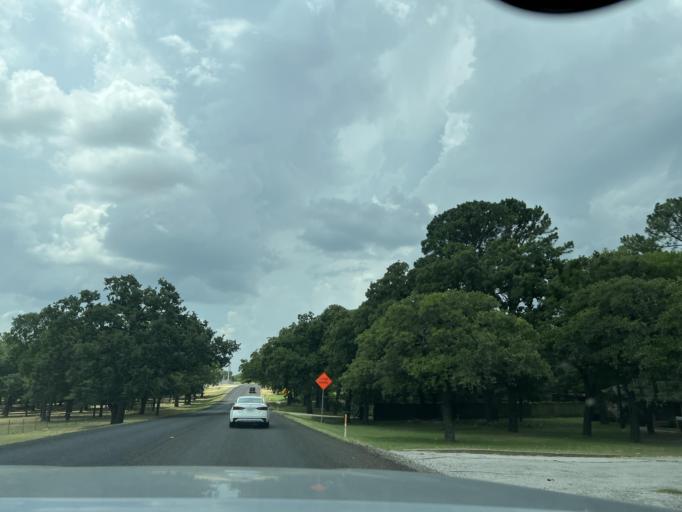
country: US
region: Texas
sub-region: Wise County
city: Decatur
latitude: 33.2030
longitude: -97.6031
